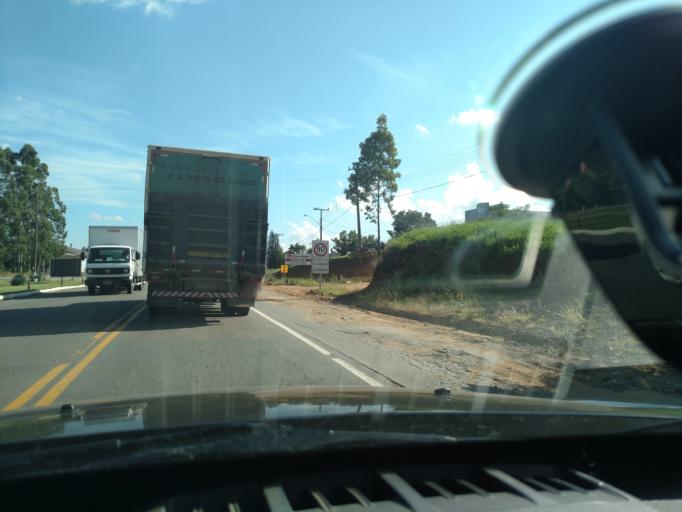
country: BR
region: Santa Catarina
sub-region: Ibirama
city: Ibirama
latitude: -27.1229
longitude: -49.5363
